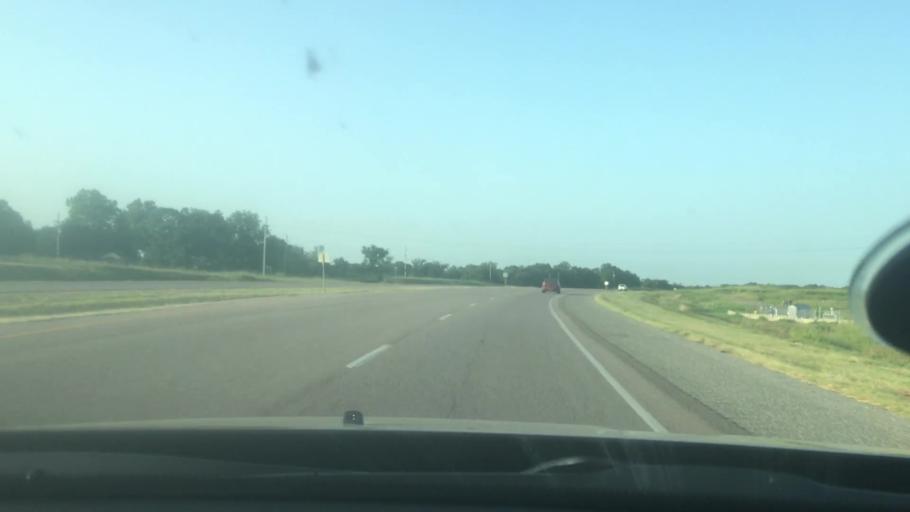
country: US
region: Oklahoma
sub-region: Pontotoc County
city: Ada
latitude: 34.8199
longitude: -96.6932
